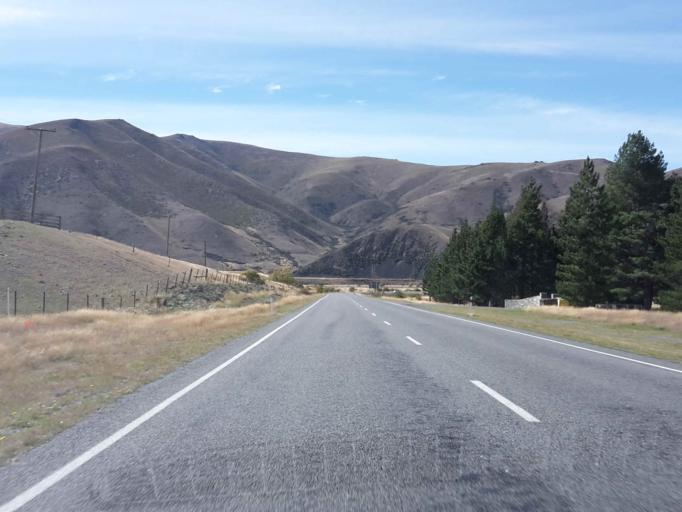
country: NZ
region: Otago
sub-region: Queenstown-Lakes District
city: Wanaka
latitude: -44.5001
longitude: 169.7524
